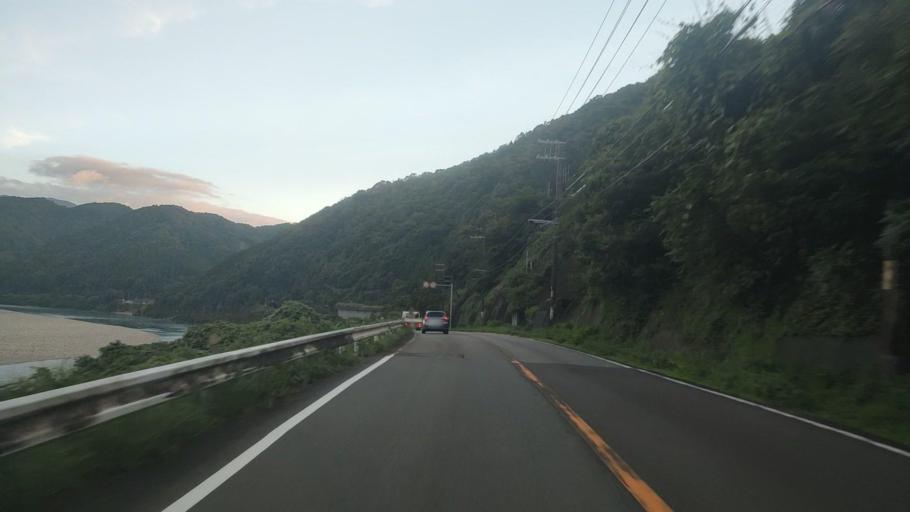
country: JP
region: Wakayama
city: Shingu
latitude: 33.8221
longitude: 135.8554
